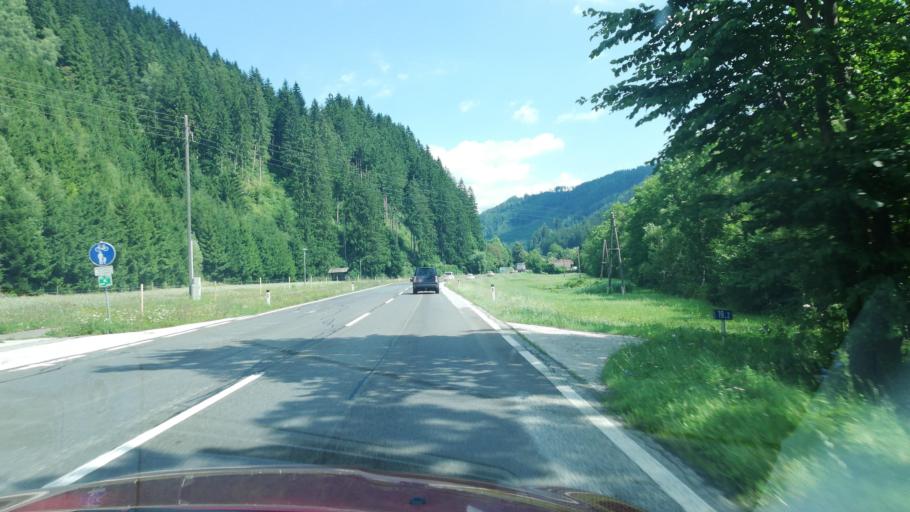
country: AT
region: Styria
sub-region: Politischer Bezirk Murau
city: Durnstein in der Steiermark
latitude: 47.0151
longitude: 14.4083
